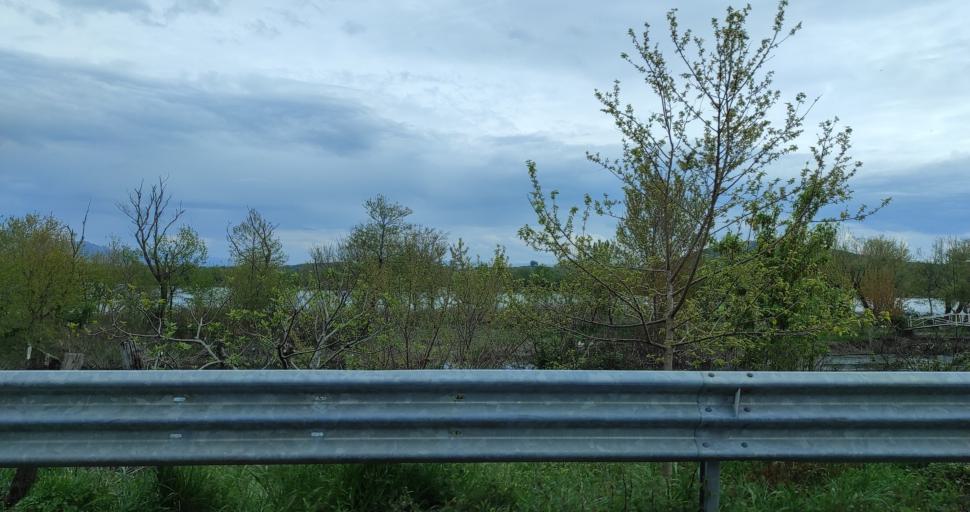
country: AL
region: Shkoder
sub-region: Rrethi i Shkodres
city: Berdica e Madhe
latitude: 42.0381
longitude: 19.4806
